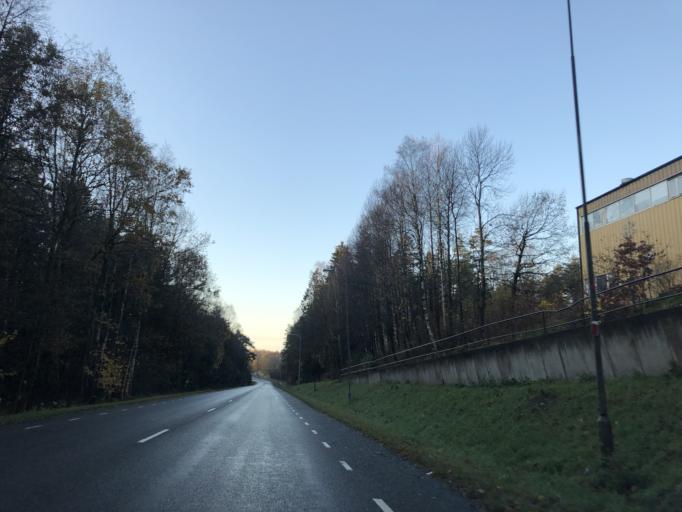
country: SE
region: Vaestra Goetaland
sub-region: Goteborg
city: Hammarkullen
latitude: 57.7805
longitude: 12.0257
